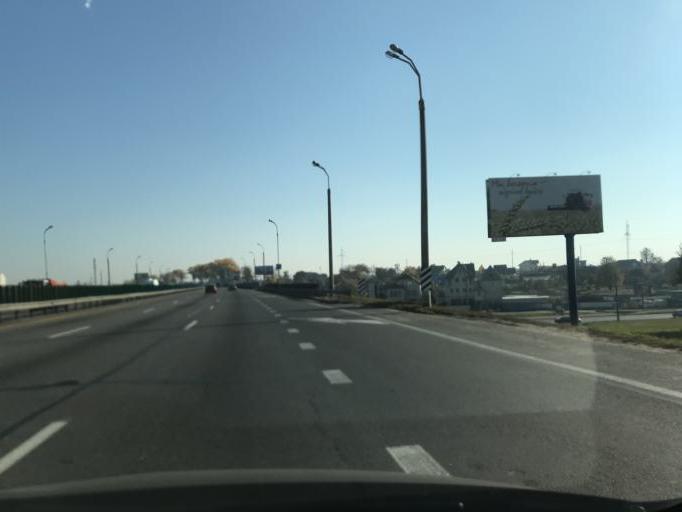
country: BY
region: Minsk
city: Malinovka
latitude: 53.8500
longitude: 27.4364
